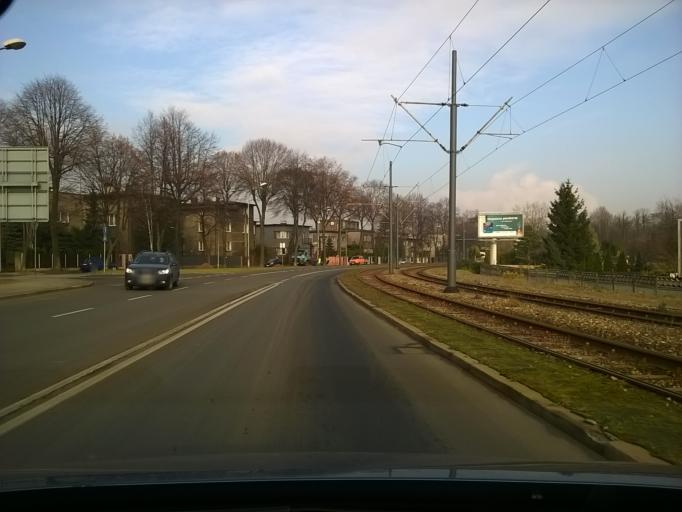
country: PL
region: Silesian Voivodeship
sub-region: Chorzow
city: Chorzow
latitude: 50.2835
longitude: 18.9487
